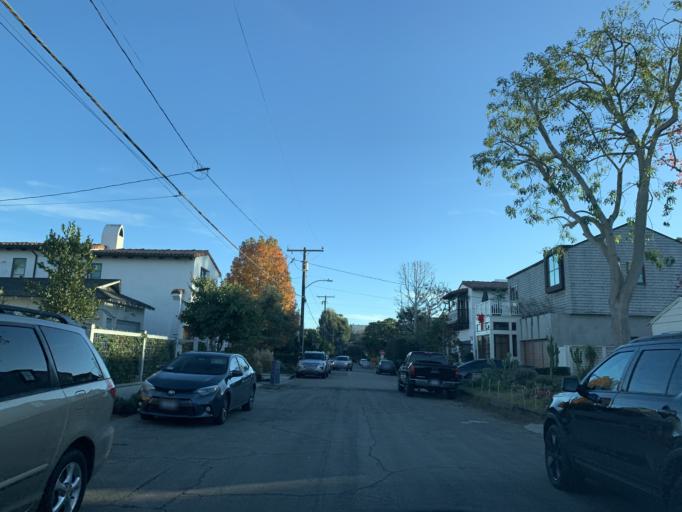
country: US
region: California
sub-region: Los Angeles County
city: Hermosa Beach
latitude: 33.8703
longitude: -118.3995
